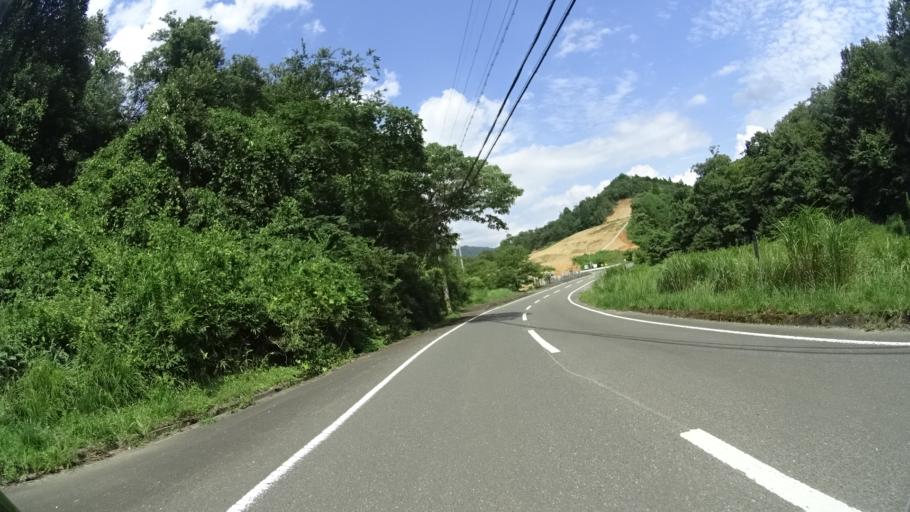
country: JP
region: Kyoto
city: Maizuru
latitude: 35.3672
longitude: 135.3286
